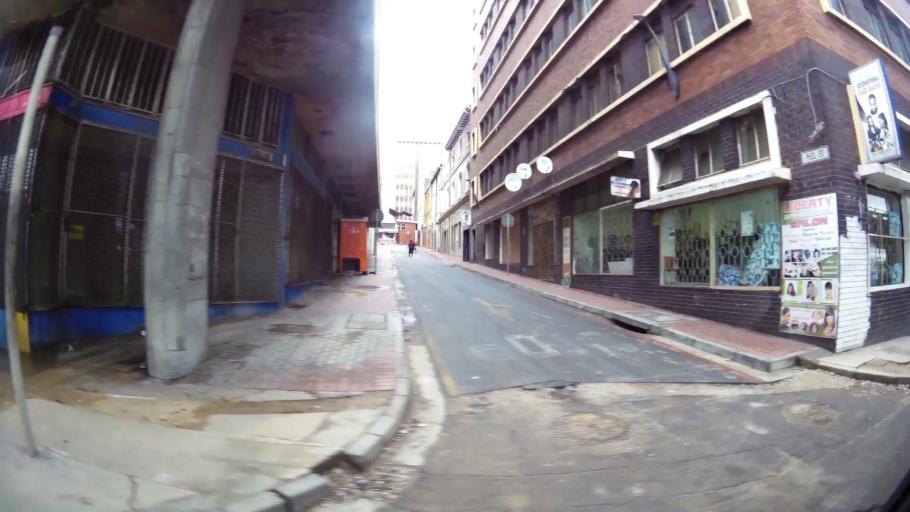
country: ZA
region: Eastern Cape
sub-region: Nelson Mandela Bay Metropolitan Municipality
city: Port Elizabeth
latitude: -33.9588
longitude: 25.6220
